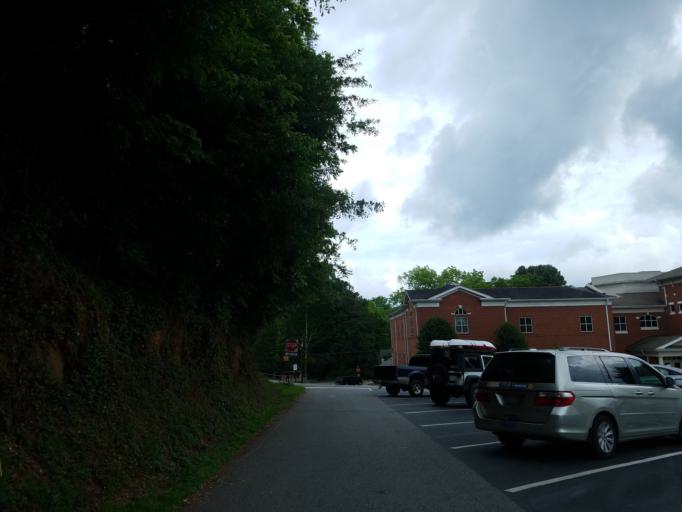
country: US
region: Georgia
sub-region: Lumpkin County
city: Dahlonega
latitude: 34.5325
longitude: -83.9830
